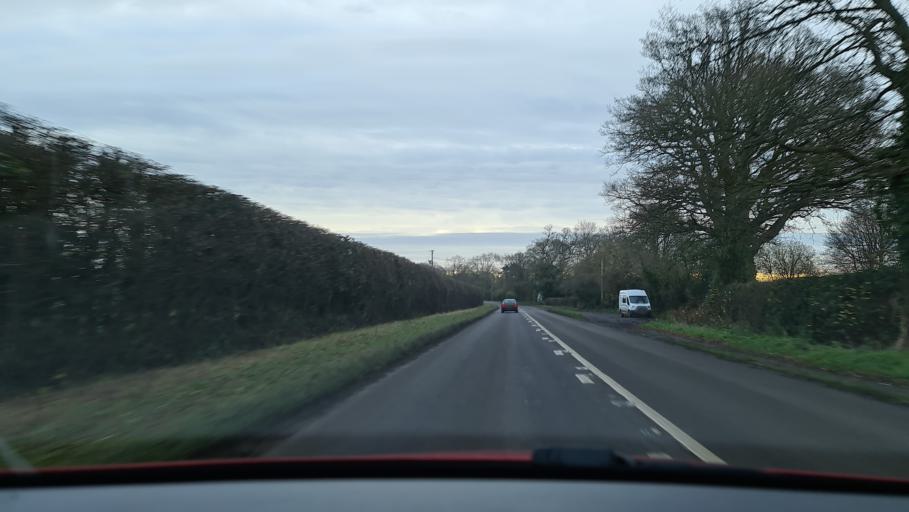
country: GB
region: England
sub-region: Buckinghamshire
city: Great Missenden
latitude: 51.7023
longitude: -0.6819
